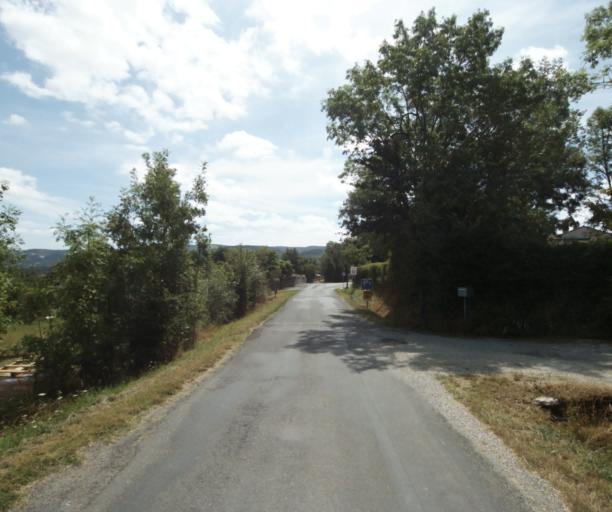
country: FR
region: Midi-Pyrenees
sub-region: Departement du Tarn
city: Soreze
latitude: 43.4719
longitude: 2.0772
